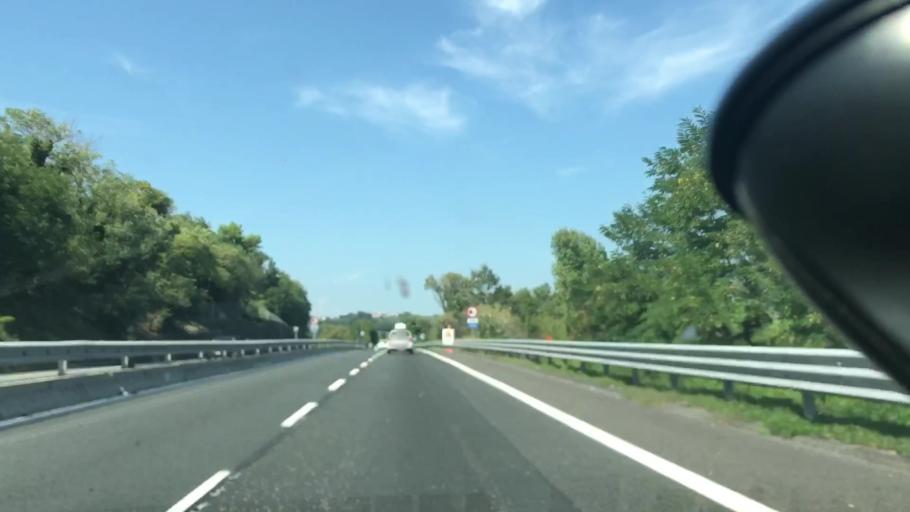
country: IT
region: Abruzzo
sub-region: Provincia di Chieti
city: Torino di Sangro
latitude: 42.2039
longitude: 14.5534
